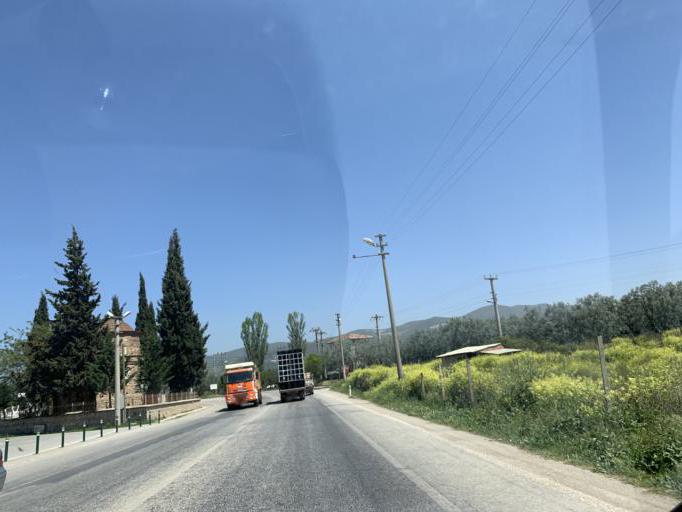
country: TR
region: Bursa
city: Iznik
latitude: 40.4206
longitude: 29.7184
